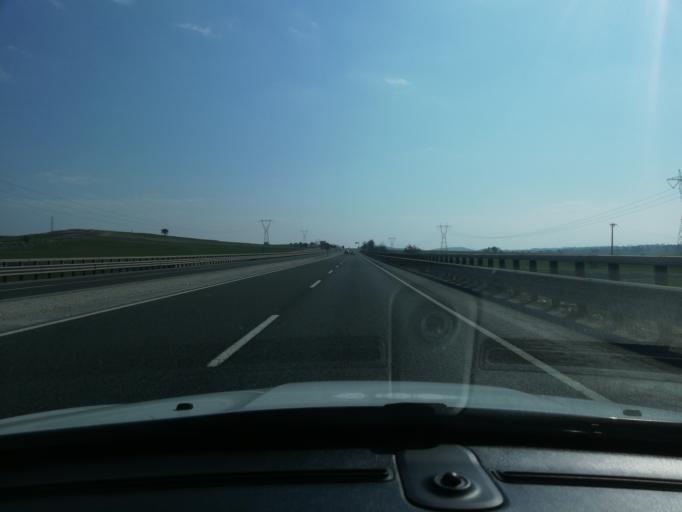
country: TR
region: Cankiri
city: Kursunlu
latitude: 40.8430
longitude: 33.1803
